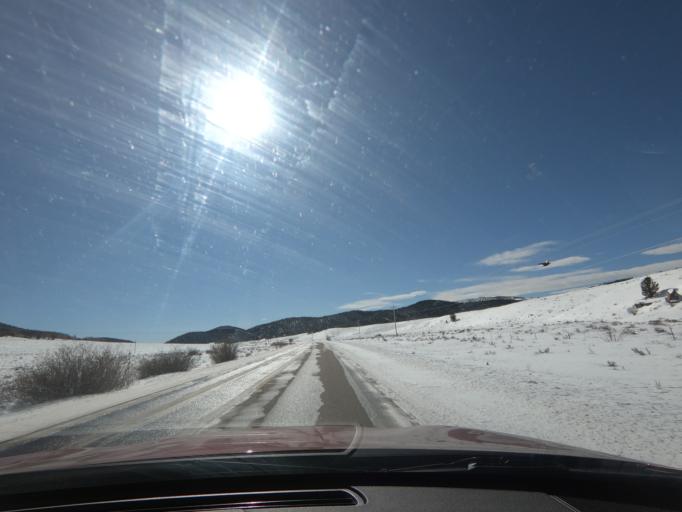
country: US
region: Colorado
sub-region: Teller County
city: Cripple Creek
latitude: 38.7757
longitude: -105.1218
